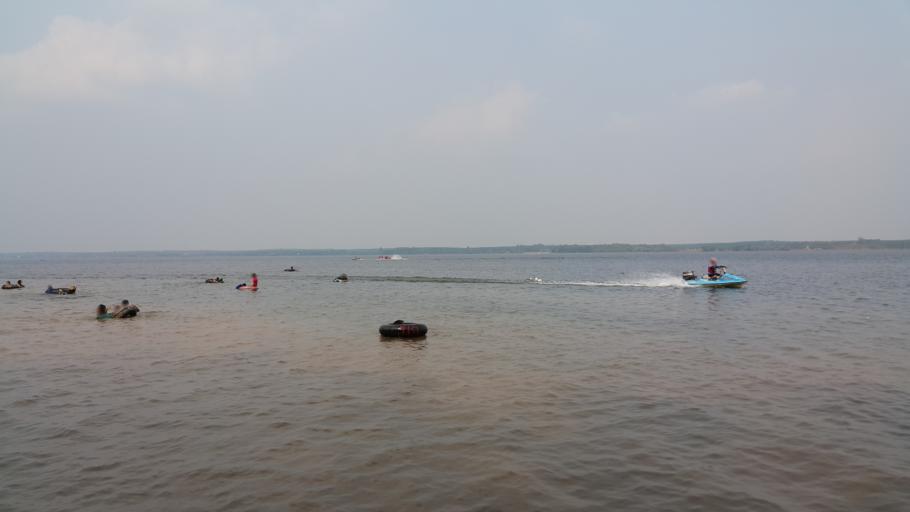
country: TH
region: Nong Khai
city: Bueng Khong Long
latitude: 17.9834
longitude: 104.0264
